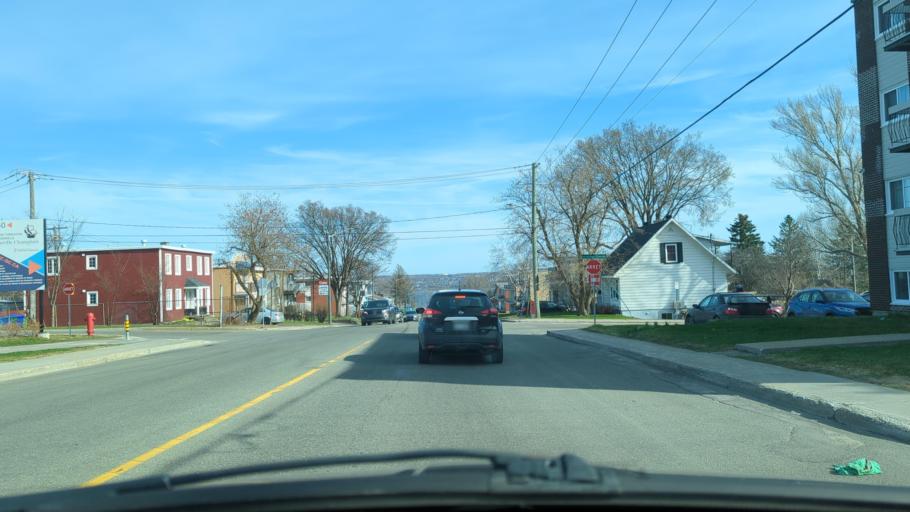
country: CA
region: Quebec
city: Quebec
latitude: 46.8594
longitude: -71.2103
